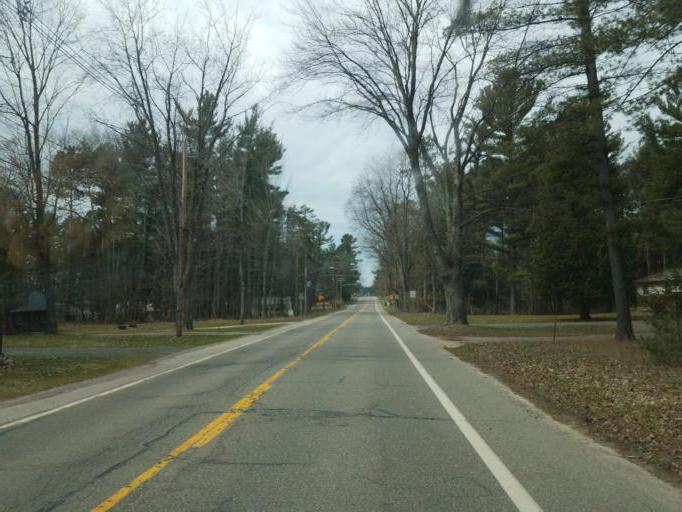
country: US
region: Michigan
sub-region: Oceana County
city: Hart
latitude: 43.7762
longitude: -86.4207
